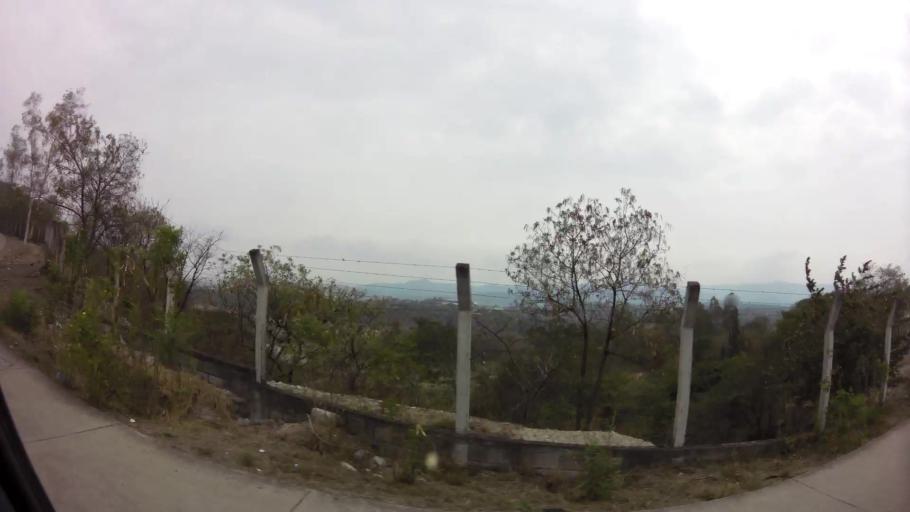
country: HN
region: Francisco Morazan
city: Tegucigalpa
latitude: 14.0705
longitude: -87.2467
